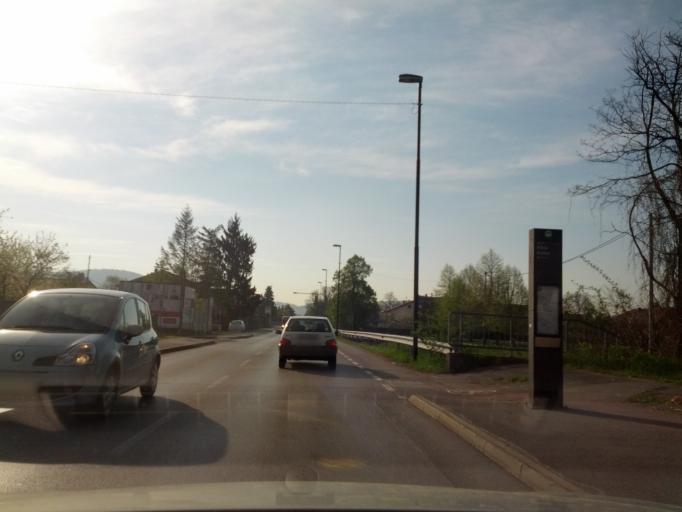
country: SI
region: Ljubljana
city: Ljubljana
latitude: 46.0291
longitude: 14.5219
